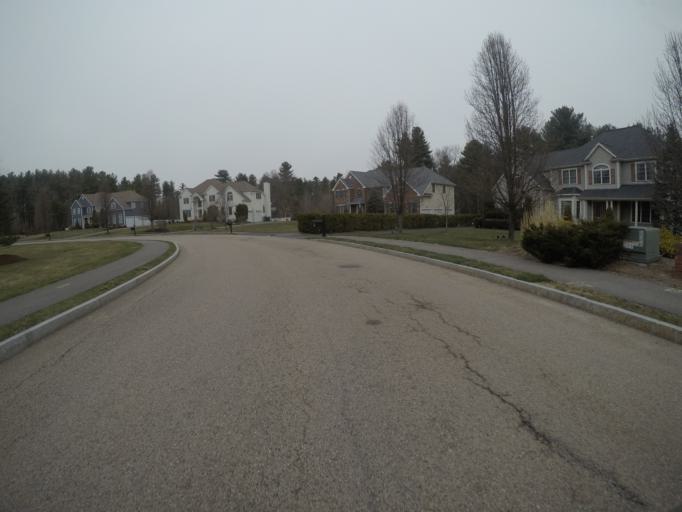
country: US
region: Massachusetts
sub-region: Bristol County
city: Easton
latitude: 42.0172
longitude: -71.1091
